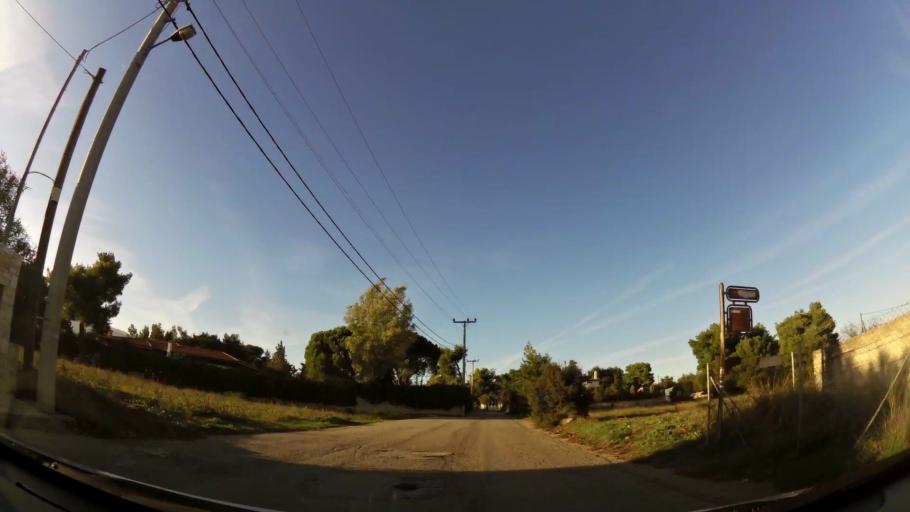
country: GR
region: Attica
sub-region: Nomarchia Anatolikis Attikis
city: Kryoneri
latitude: 38.1297
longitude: 23.8251
